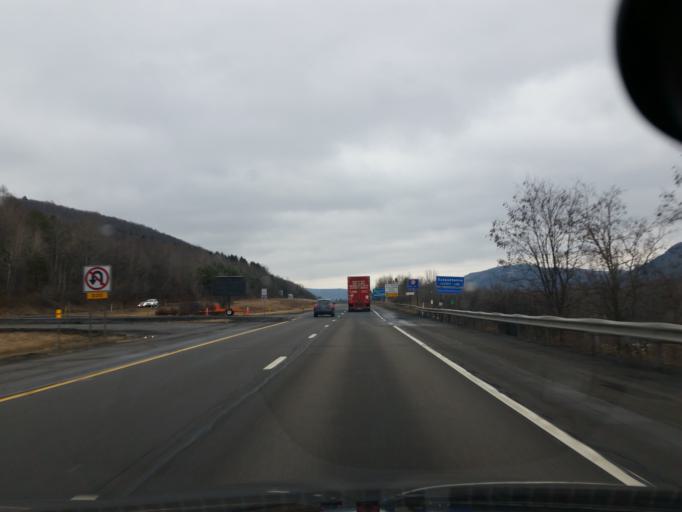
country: US
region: Pennsylvania
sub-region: Susquehanna County
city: Hallstead
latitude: 41.9986
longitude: -75.7525
